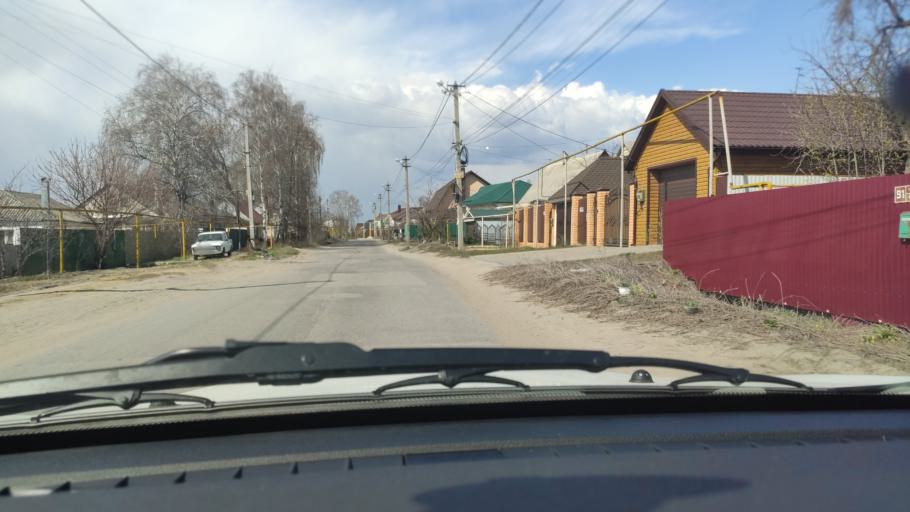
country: RU
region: Voronezj
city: Podgornoye
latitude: 51.7373
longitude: 39.1567
